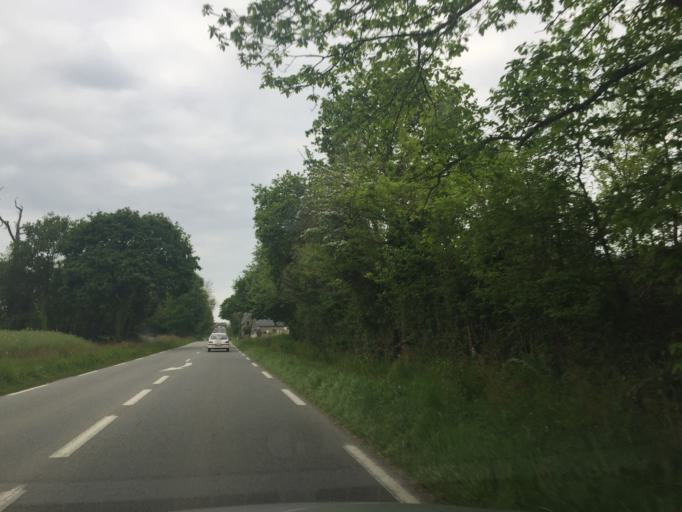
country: FR
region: Brittany
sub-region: Departement des Cotes-d'Armor
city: Saint-Cast-le-Guildo
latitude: 48.6126
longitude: -2.2713
